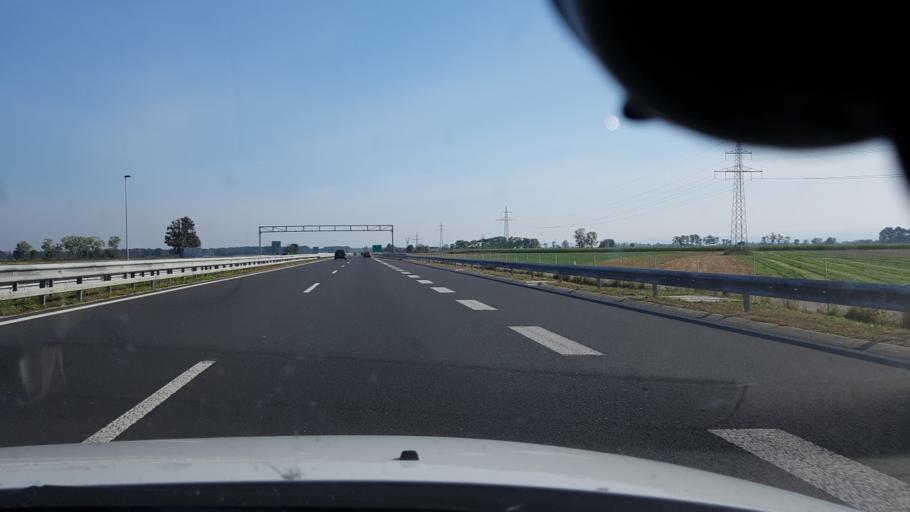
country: SI
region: Hoce-Slivnica
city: Hotinja Vas
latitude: 46.4724
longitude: 15.6791
